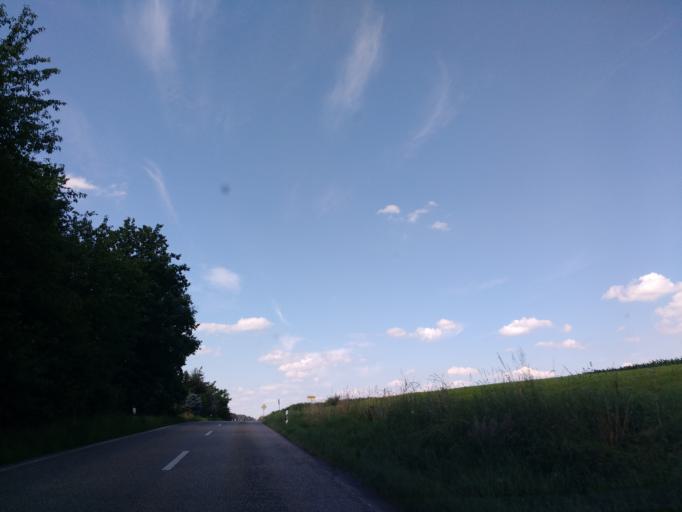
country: DE
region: Bavaria
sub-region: Upper Bavaria
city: Taufkirchen
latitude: 48.1180
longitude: 12.4183
